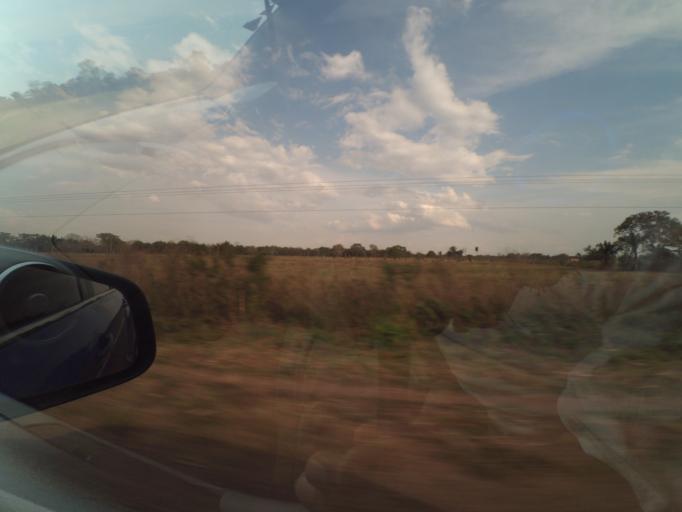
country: BO
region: Santa Cruz
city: Montero
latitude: -17.2635
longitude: -63.0646
